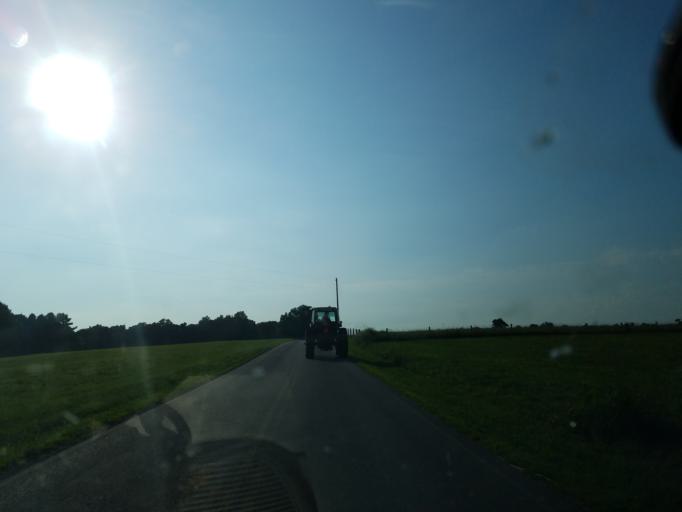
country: US
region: Ohio
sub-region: Adams County
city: West Union
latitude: 38.8844
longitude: -83.5033
